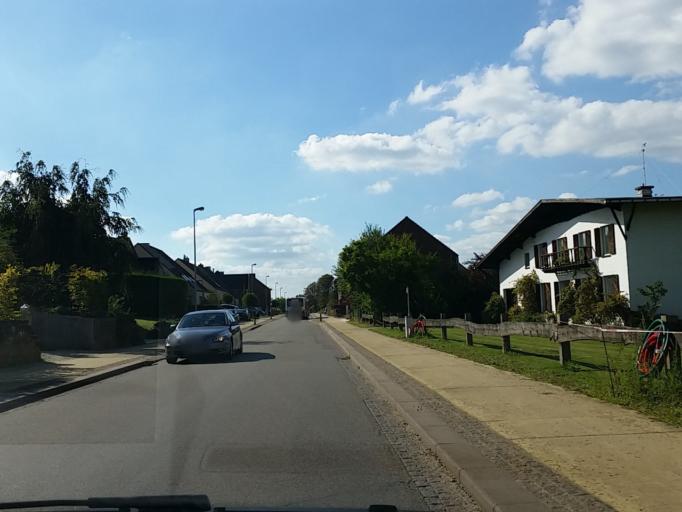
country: BE
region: Flanders
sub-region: Provincie Vlaams-Brabant
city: Holsbeek
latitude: 50.9255
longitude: 4.7993
